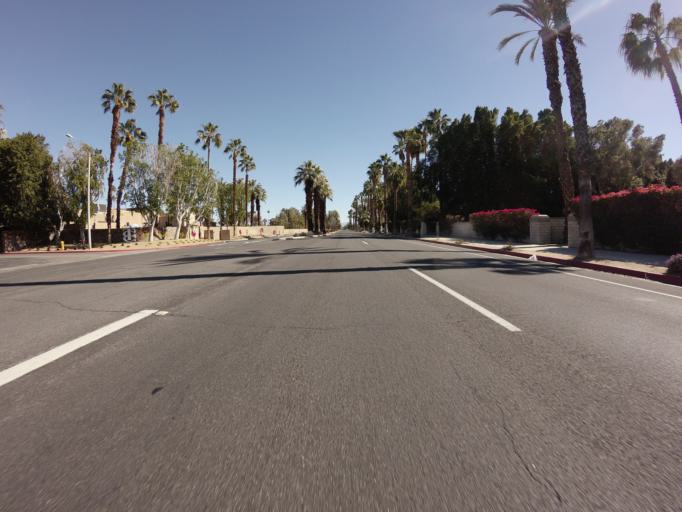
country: US
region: California
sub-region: Riverside County
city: Cathedral City
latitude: 33.7724
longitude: -116.4382
